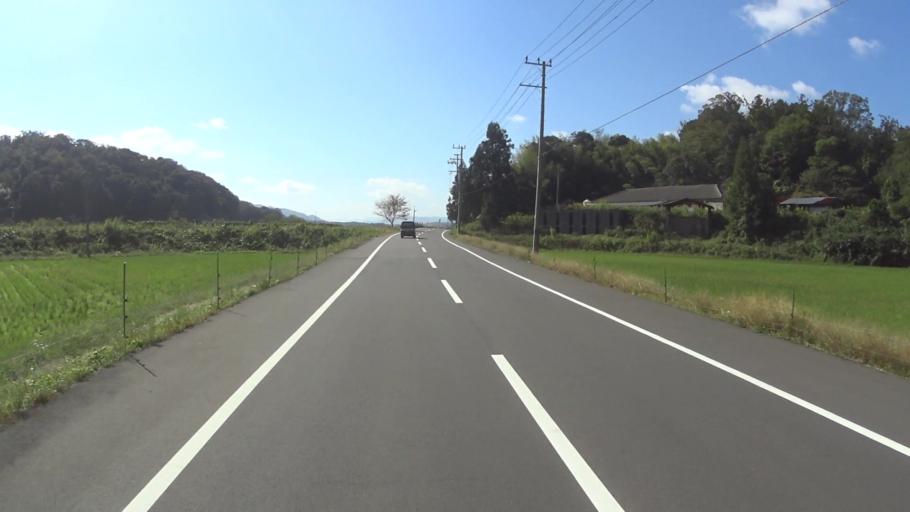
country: JP
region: Kyoto
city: Miyazu
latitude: 35.6942
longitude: 135.0982
